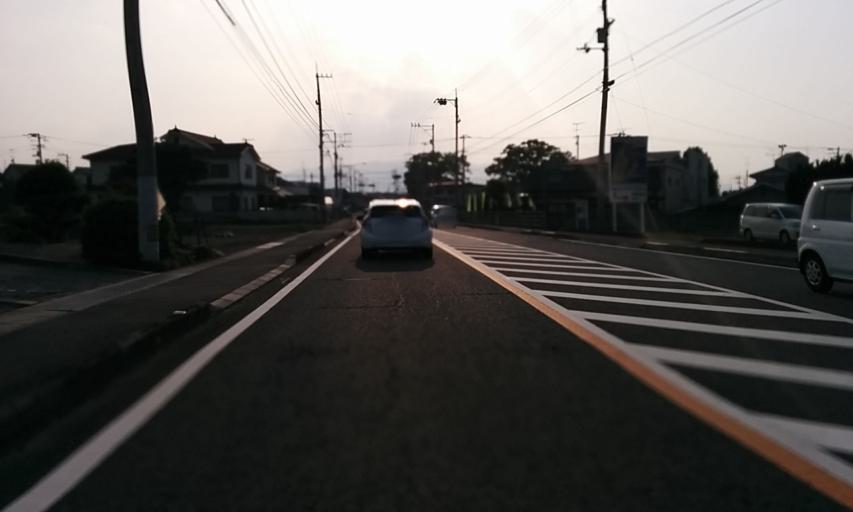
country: JP
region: Ehime
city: Saijo
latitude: 33.8954
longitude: 133.1317
